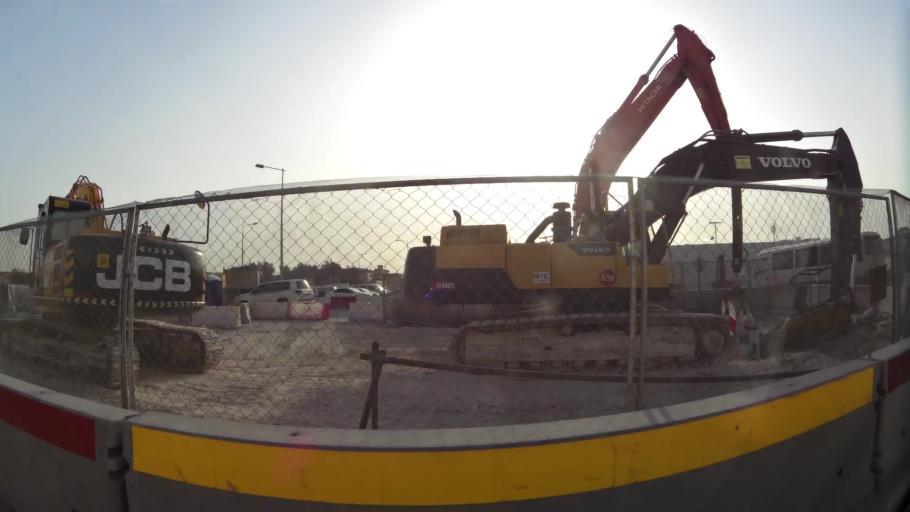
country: QA
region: Baladiyat ar Rayyan
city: Ar Rayyan
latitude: 25.2455
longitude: 51.4537
